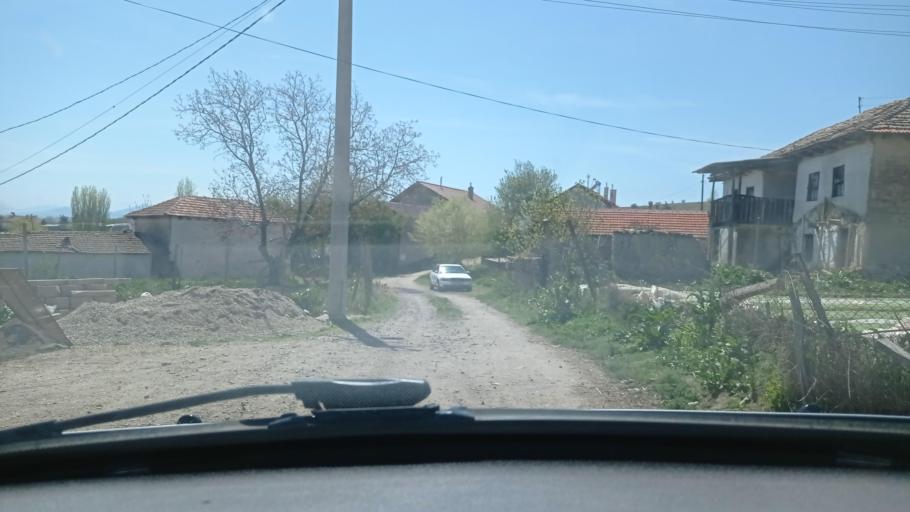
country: MK
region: Lozovo
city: Lozovo
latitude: 41.8055
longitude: 21.8687
